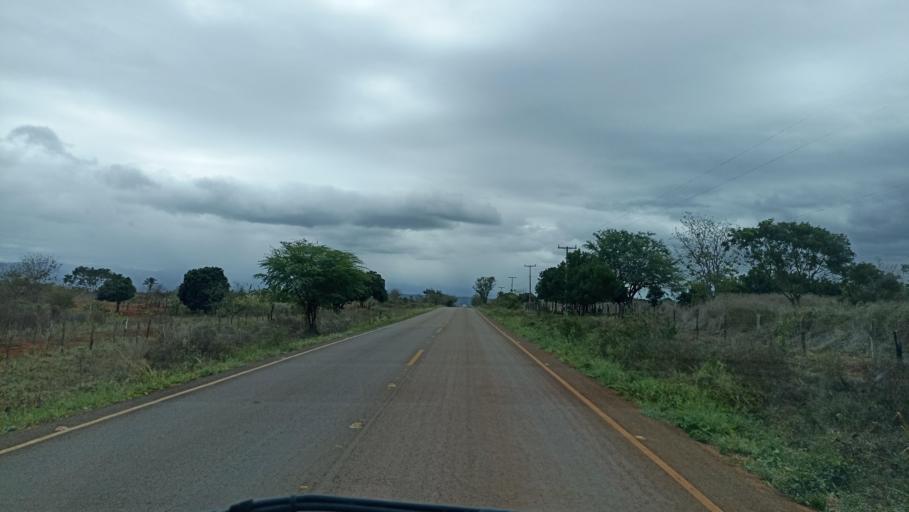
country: BR
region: Bahia
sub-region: Andarai
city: Vera Cruz
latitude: -12.9702
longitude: -41.0278
